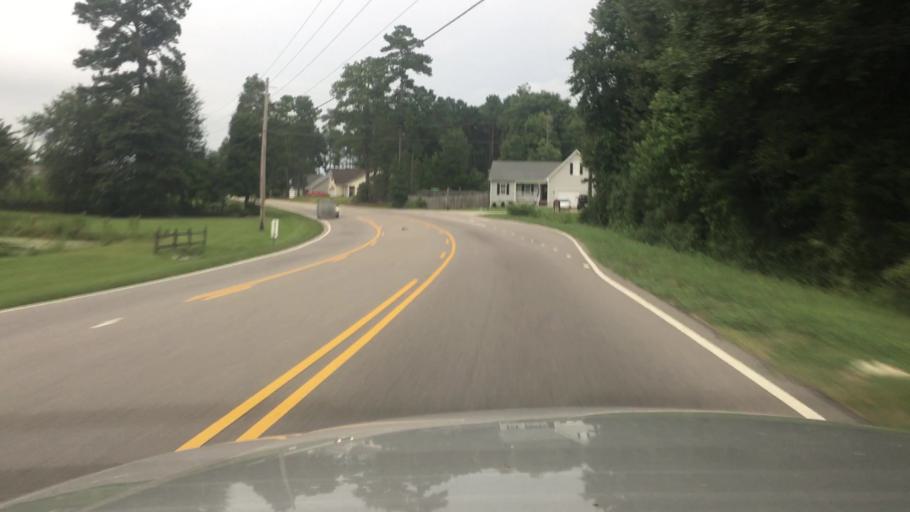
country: US
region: North Carolina
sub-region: Hoke County
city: Rockfish
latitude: 34.9673
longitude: -79.0527
